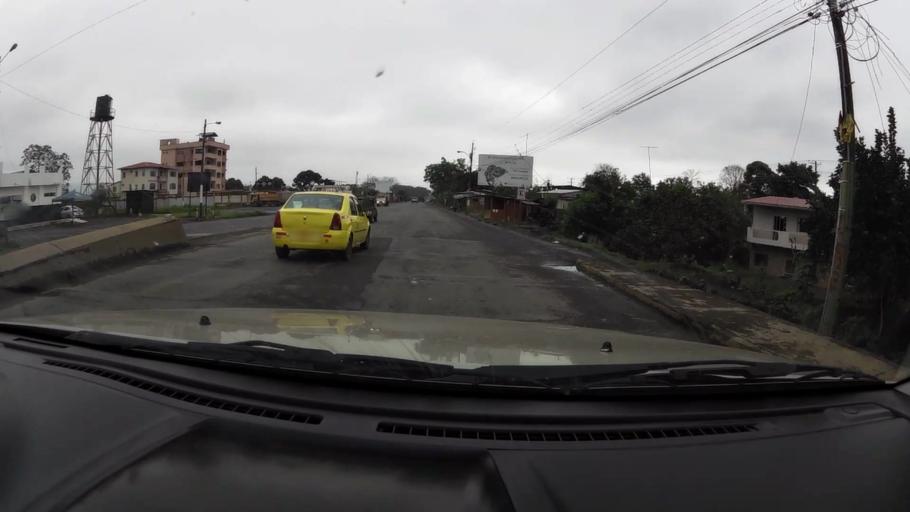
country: EC
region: Guayas
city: Balao
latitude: -3.0780
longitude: -79.7553
